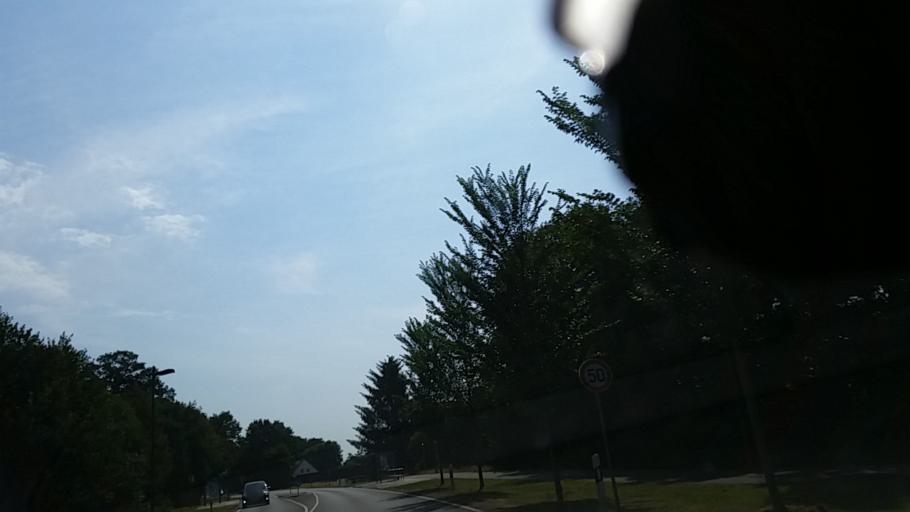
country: DE
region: Lower Saxony
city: Diepholz
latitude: 52.6101
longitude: 8.3936
